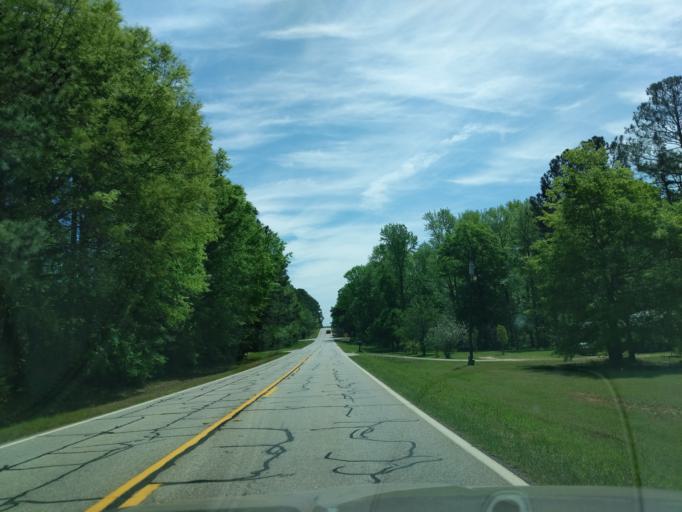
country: US
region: Georgia
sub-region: Columbia County
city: Appling
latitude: 33.6121
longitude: -82.3577
